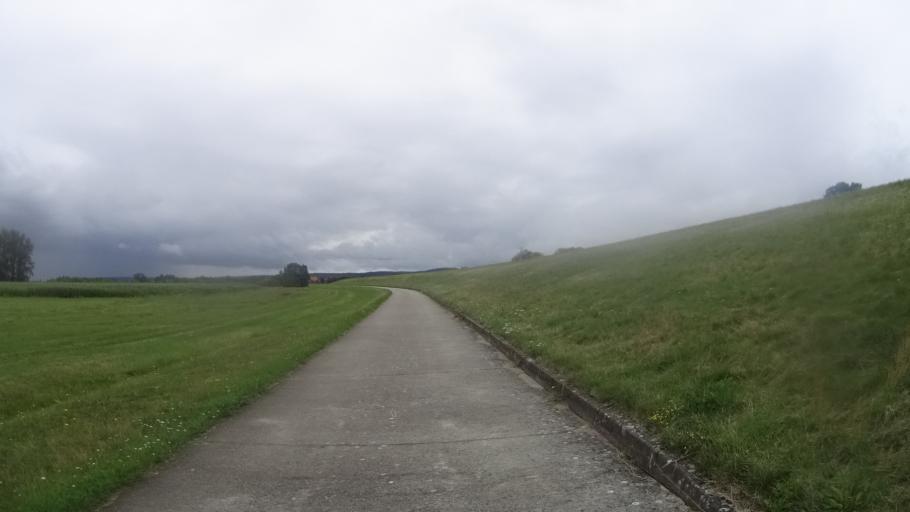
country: DE
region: Lower Saxony
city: Tosterglope
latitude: 53.2687
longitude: 10.8286
